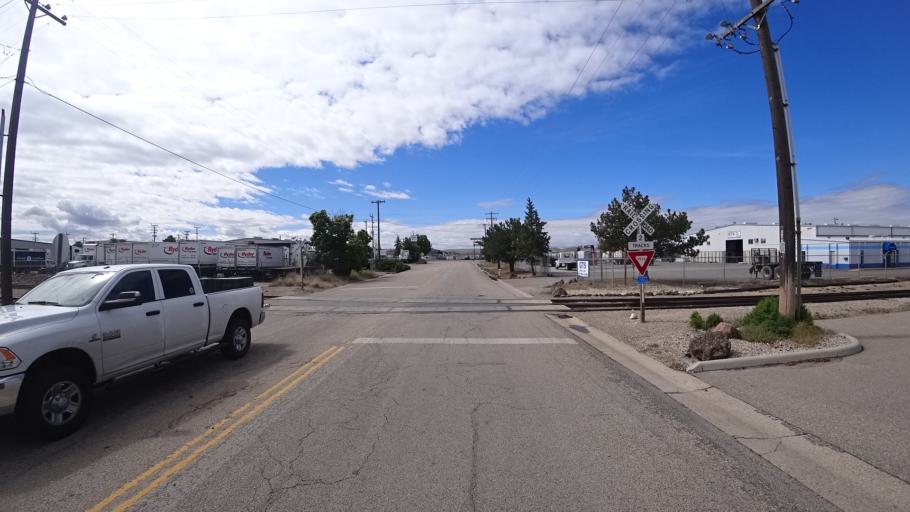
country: US
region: Idaho
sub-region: Ada County
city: Boise
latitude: 43.5616
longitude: -116.1987
